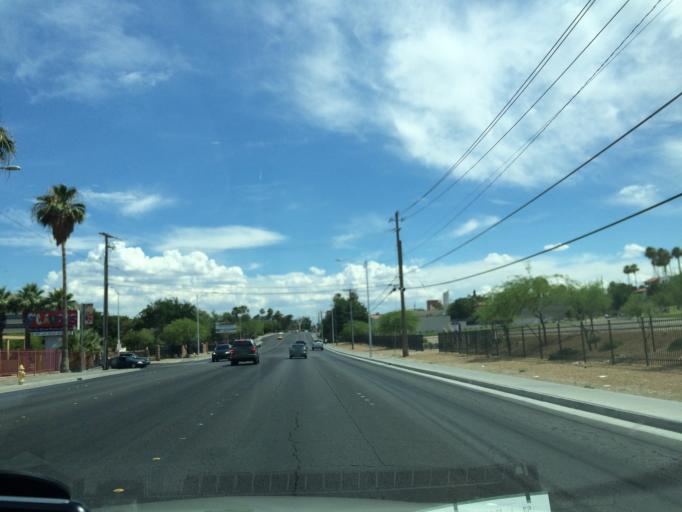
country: US
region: Nevada
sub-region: Clark County
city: Las Vegas
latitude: 36.1854
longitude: -115.1341
